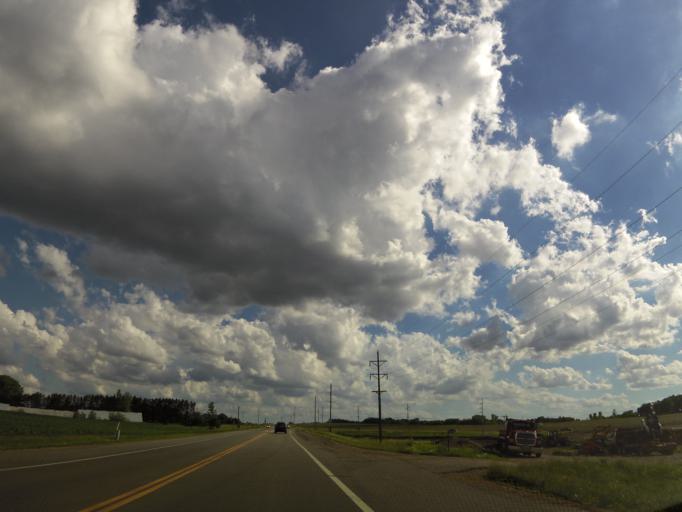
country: US
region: Minnesota
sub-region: Carver County
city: Waconia
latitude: 44.8645
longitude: -93.8165
